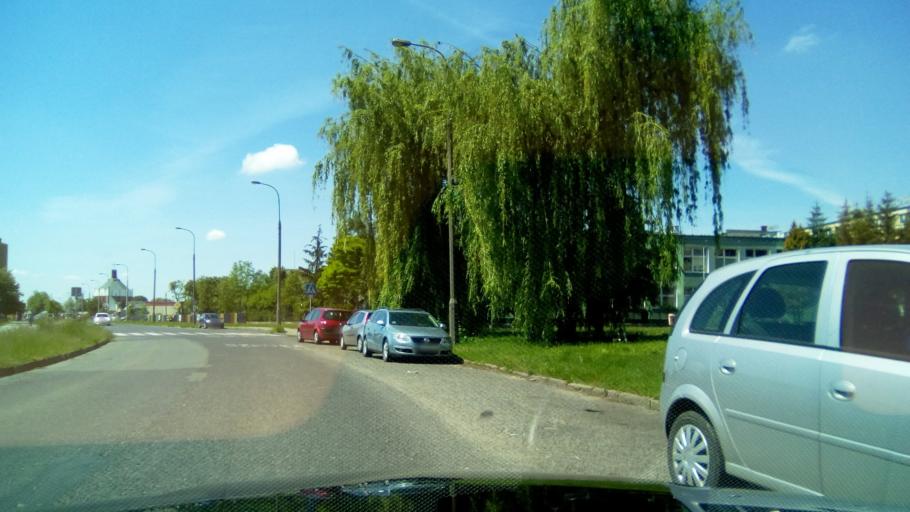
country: PL
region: Greater Poland Voivodeship
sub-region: Powiat gnieznienski
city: Gniezno
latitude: 52.5490
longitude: 17.6109
